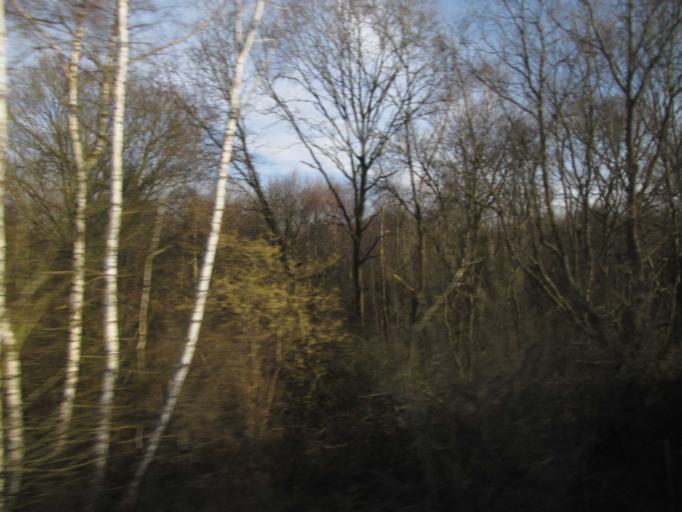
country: GB
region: England
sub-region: Surrey
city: Normandy
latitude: 51.2456
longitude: -0.6438
